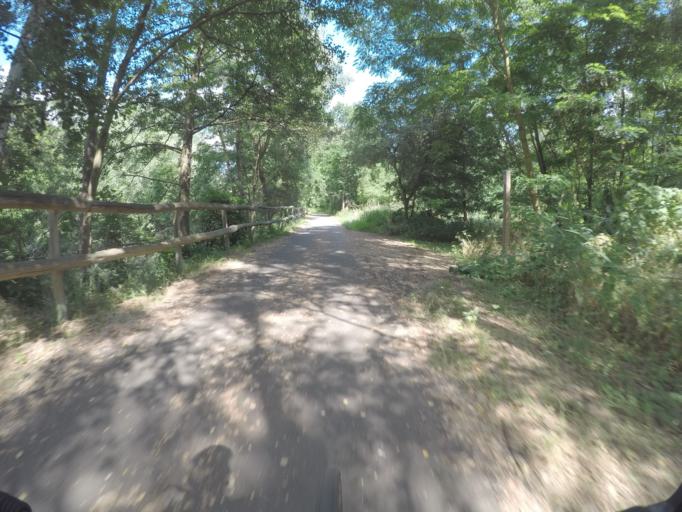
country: DE
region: Brandenburg
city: Roskow
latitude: 52.4445
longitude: 12.7435
